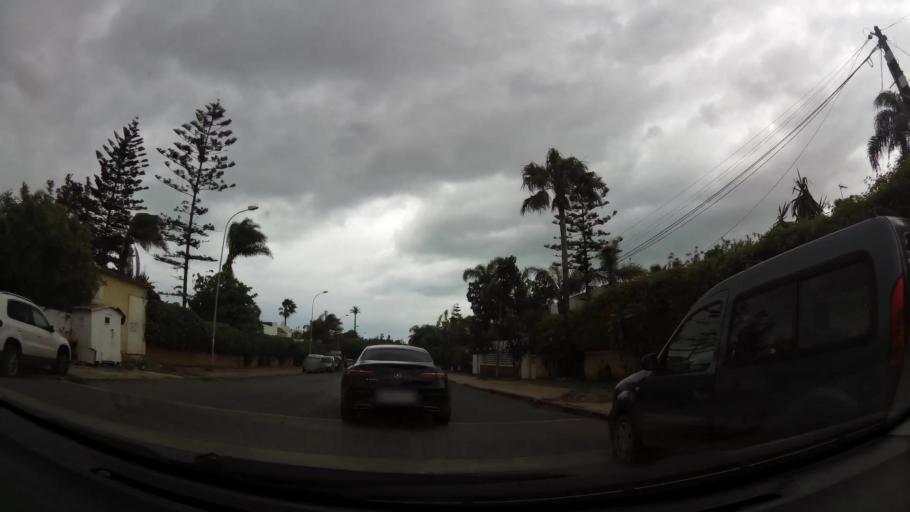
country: MA
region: Grand Casablanca
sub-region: Casablanca
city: Casablanca
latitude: 33.5799
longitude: -7.6618
